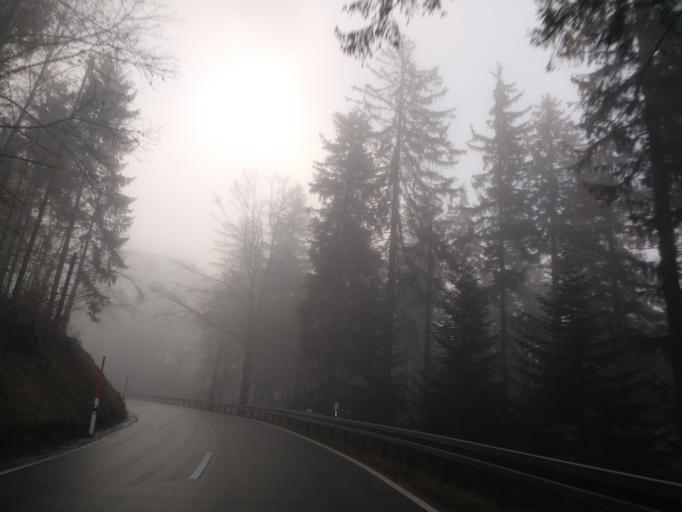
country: DE
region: Baden-Wuerttemberg
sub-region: Freiburg Region
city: Seebach
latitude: 48.5798
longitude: 8.2072
